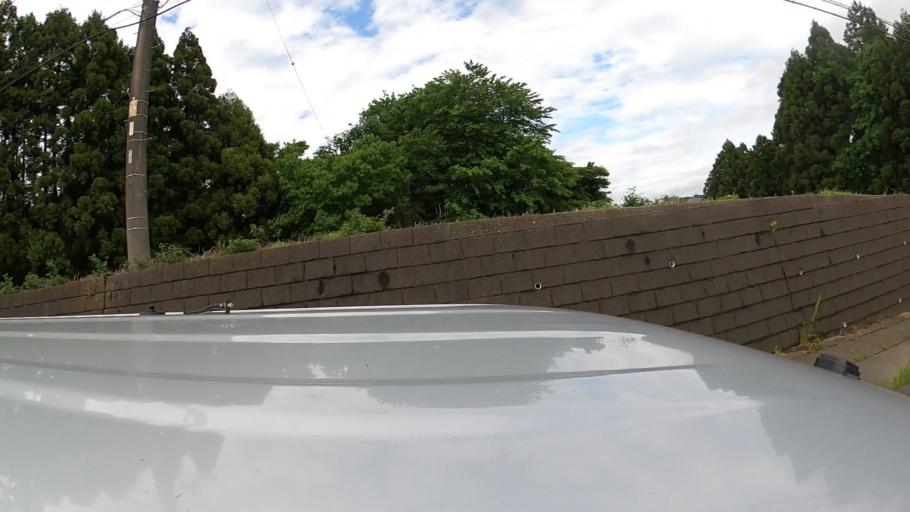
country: JP
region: Ibaraki
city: Ushiku
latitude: 35.9678
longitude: 140.1894
